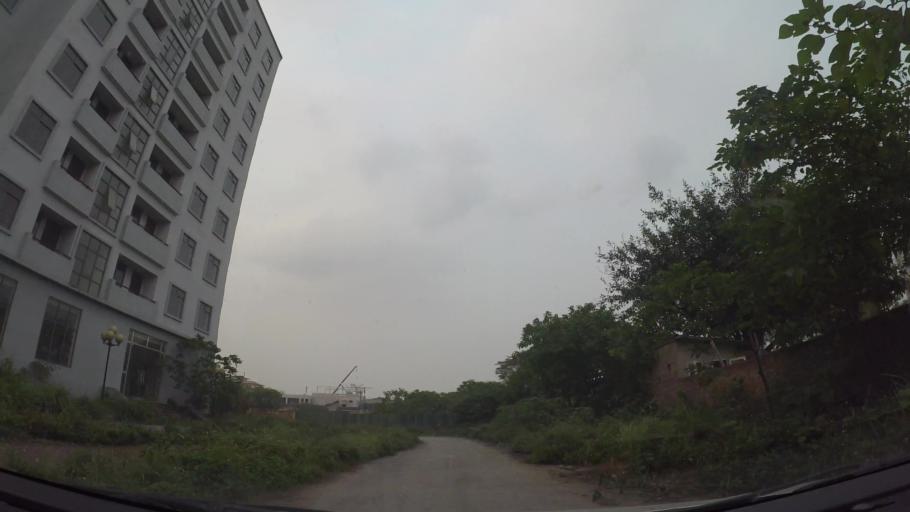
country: VN
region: Ha Noi
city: Cau Dien
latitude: 21.0417
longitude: 105.7554
